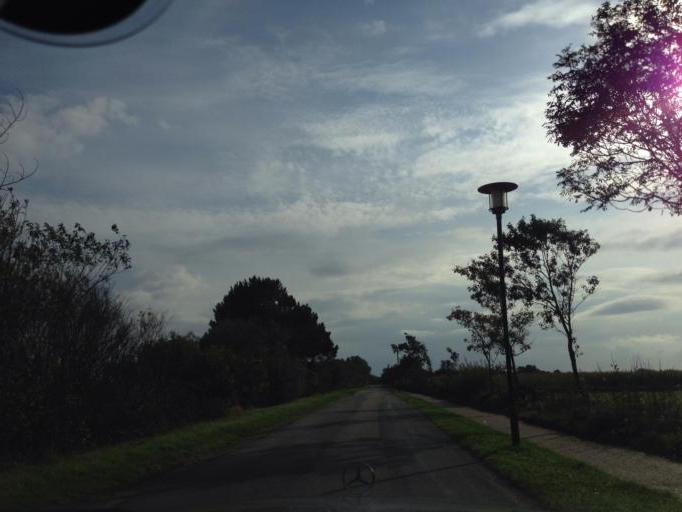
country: DE
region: Schleswig-Holstein
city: Nieblum
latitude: 54.6856
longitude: 8.4933
